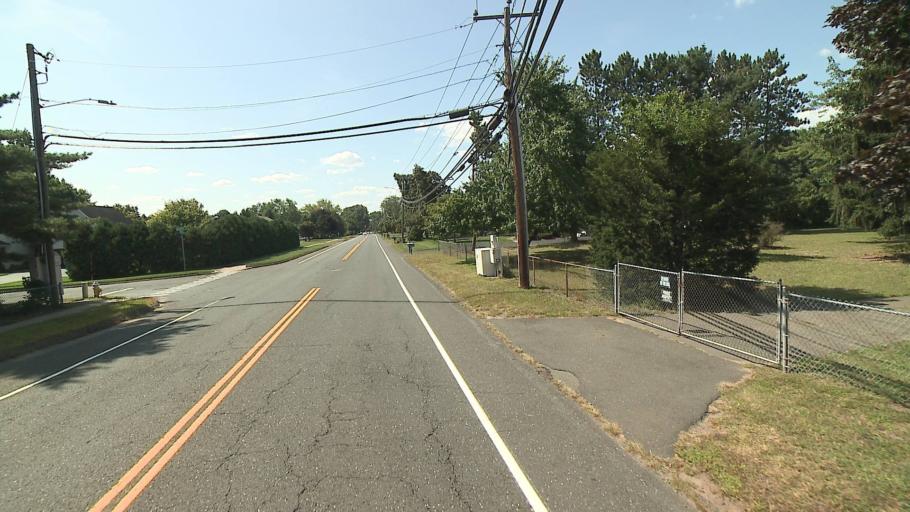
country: US
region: Connecticut
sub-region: Hartford County
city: Windsor Locks
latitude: 41.9265
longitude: -72.6520
